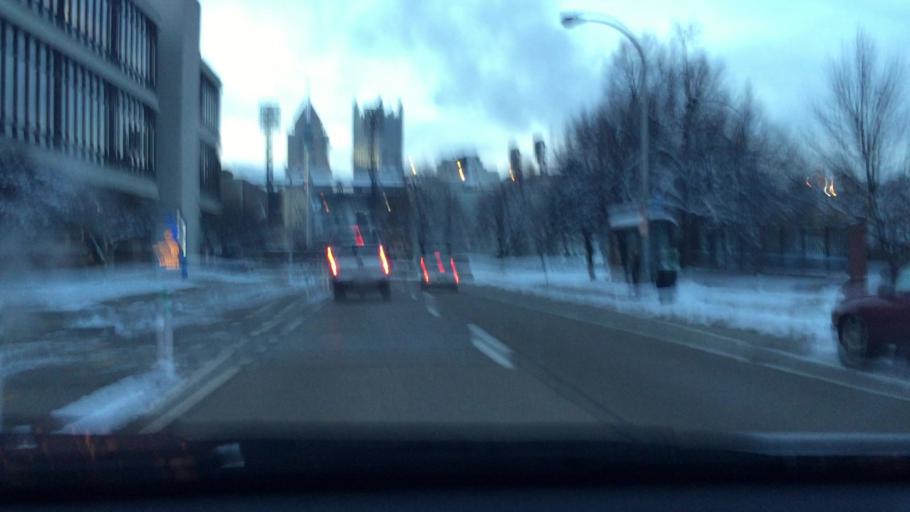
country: US
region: Pennsylvania
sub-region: Allegheny County
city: Pittsburgh
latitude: 40.4507
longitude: -80.0072
